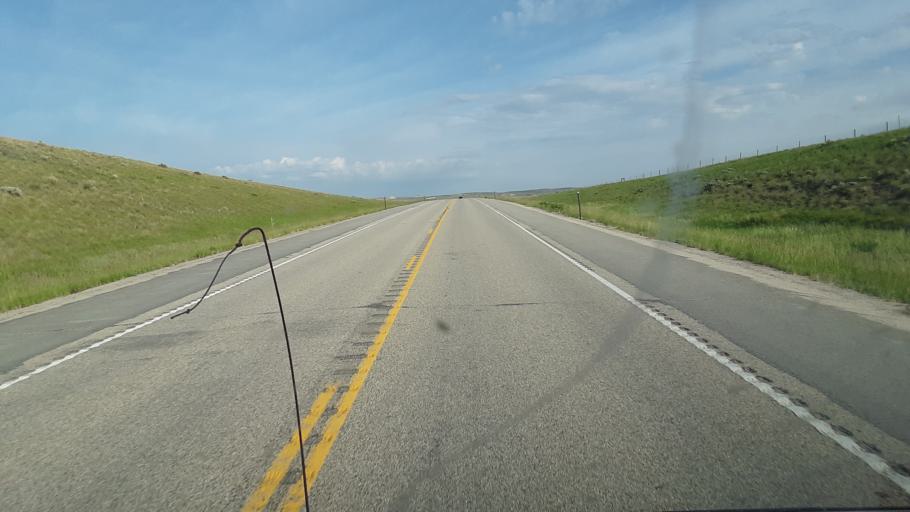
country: US
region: Wyoming
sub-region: Natrona County
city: Mills
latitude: 43.0371
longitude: -107.0254
